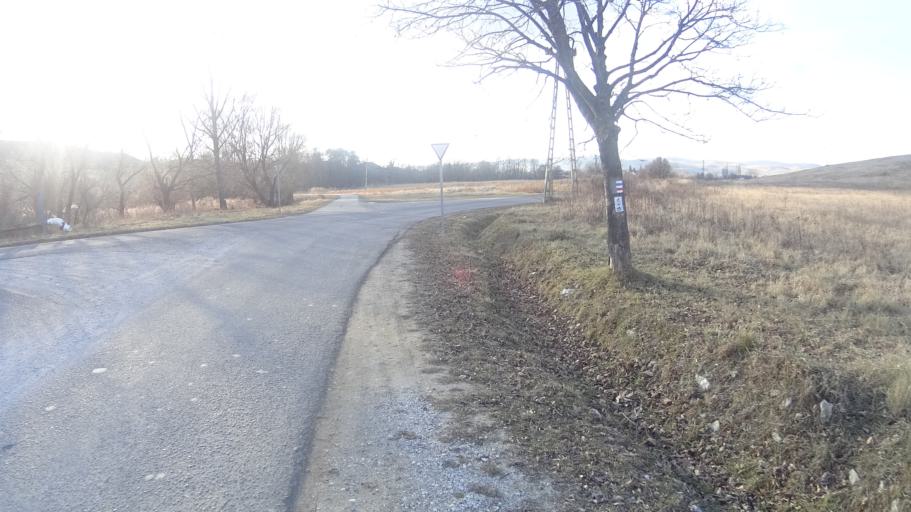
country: HU
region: Heves
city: Belapatfalva
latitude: 48.0576
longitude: 20.3628
